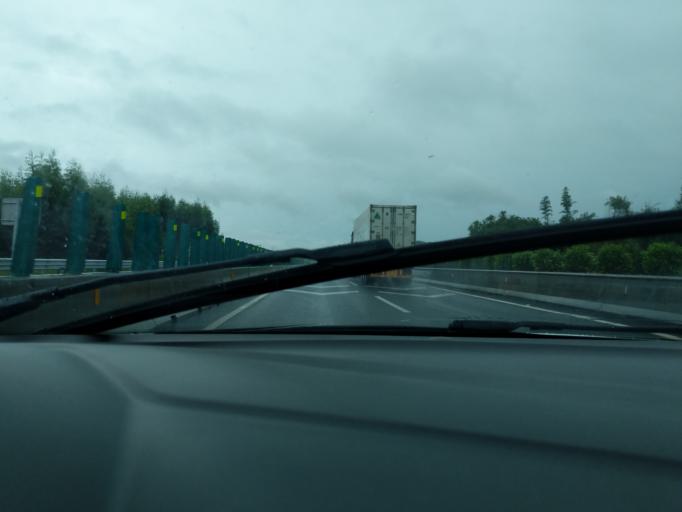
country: CN
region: Guangdong
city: Liangxi
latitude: 22.2664
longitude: 112.3220
